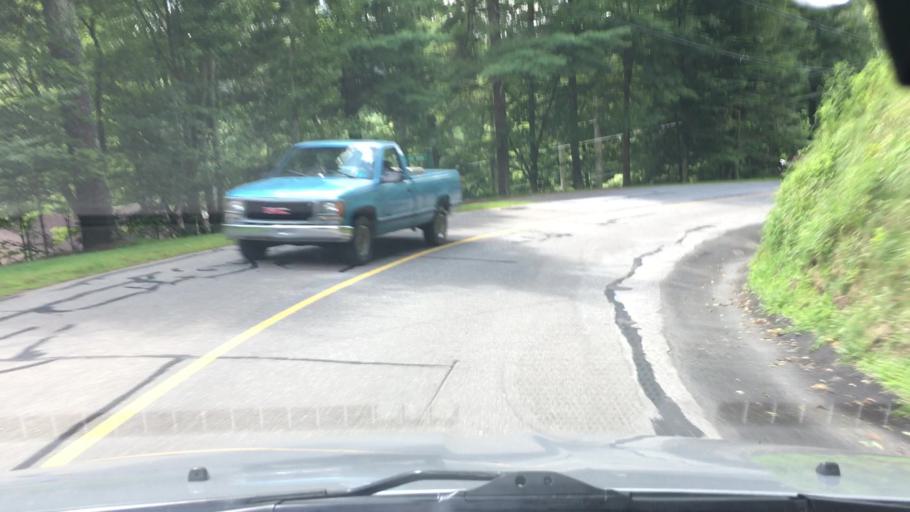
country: US
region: North Carolina
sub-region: Madison County
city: Mars Hill
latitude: 35.9659
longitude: -82.5092
